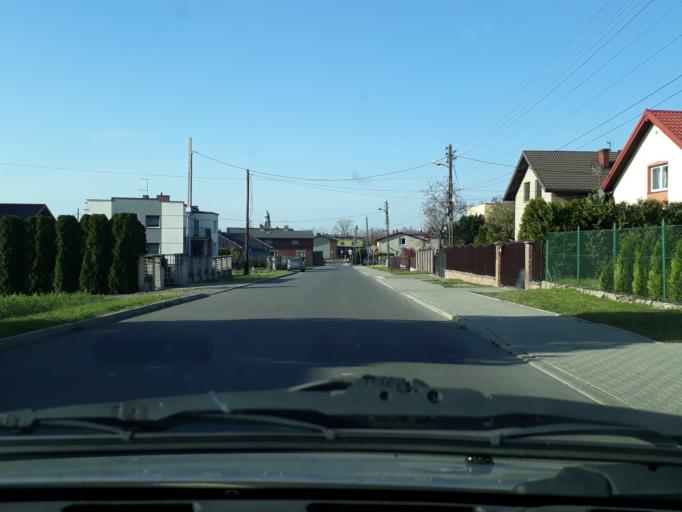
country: PL
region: Silesian Voivodeship
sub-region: Powiat tarnogorski
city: Tarnowskie Gory
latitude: 50.4224
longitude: 18.8792
